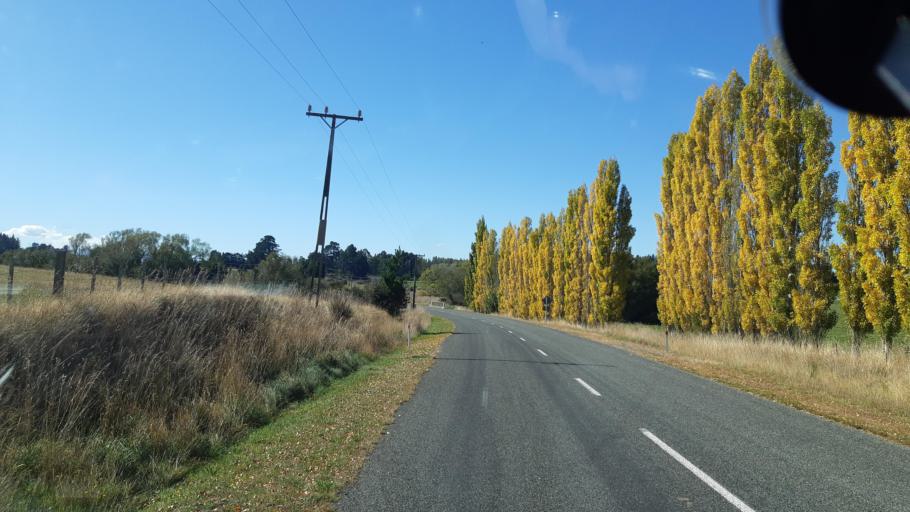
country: NZ
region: Southland
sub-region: Southland District
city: Winton
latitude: -45.8993
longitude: 168.5475
